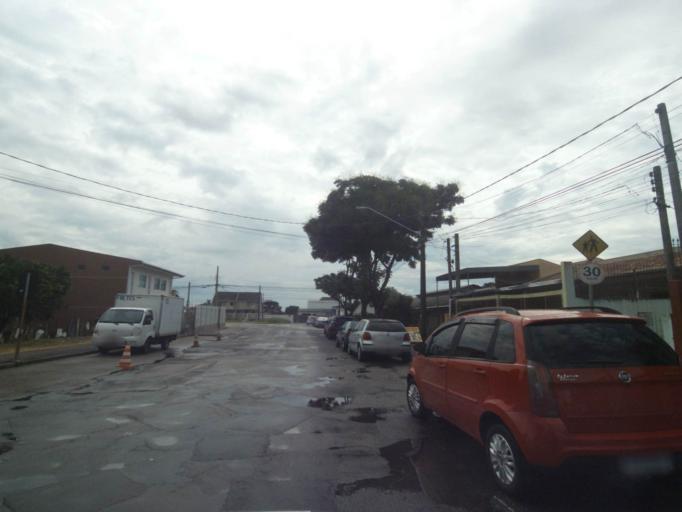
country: BR
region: Parana
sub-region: Pinhais
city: Pinhais
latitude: -25.4685
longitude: -49.2073
